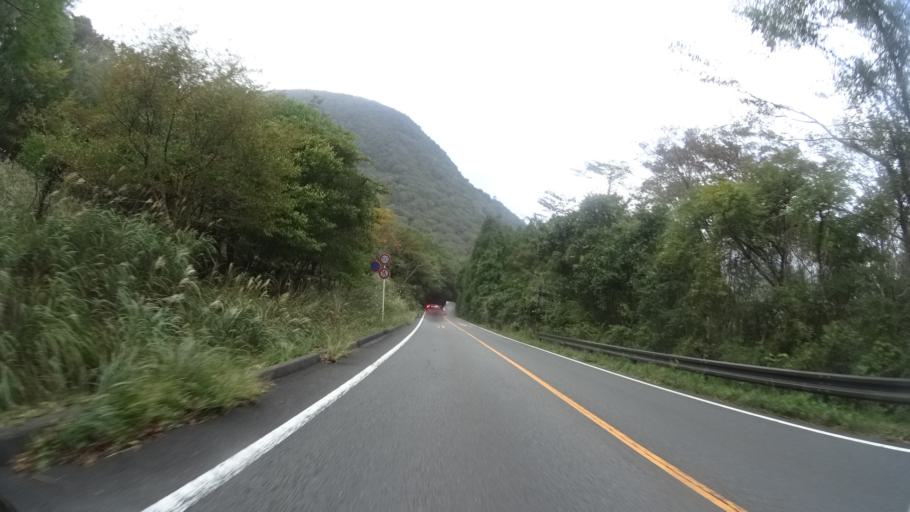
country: JP
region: Oita
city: Beppu
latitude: 33.2688
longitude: 131.4079
